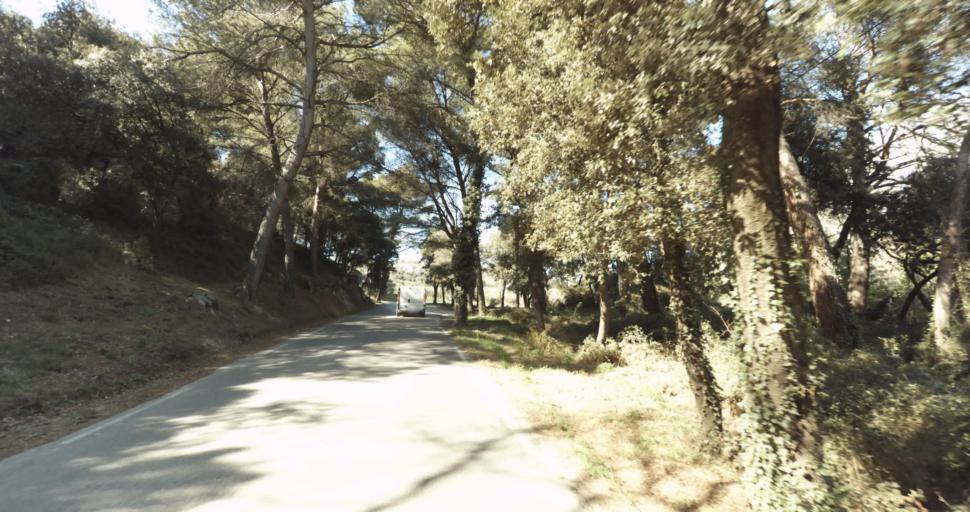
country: FR
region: Provence-Alpes-Cote d'Azur
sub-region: Departement des Bouches-du-Rhone
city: Pelissanne
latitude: 43.6492
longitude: 5.1807
